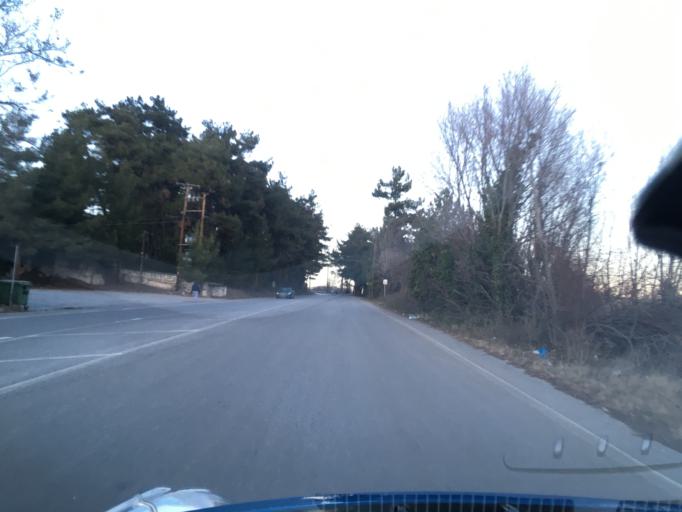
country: GR
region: West Macedonia
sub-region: Nomos Kozanis
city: Kozani
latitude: 40.2749
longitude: 21.7820
